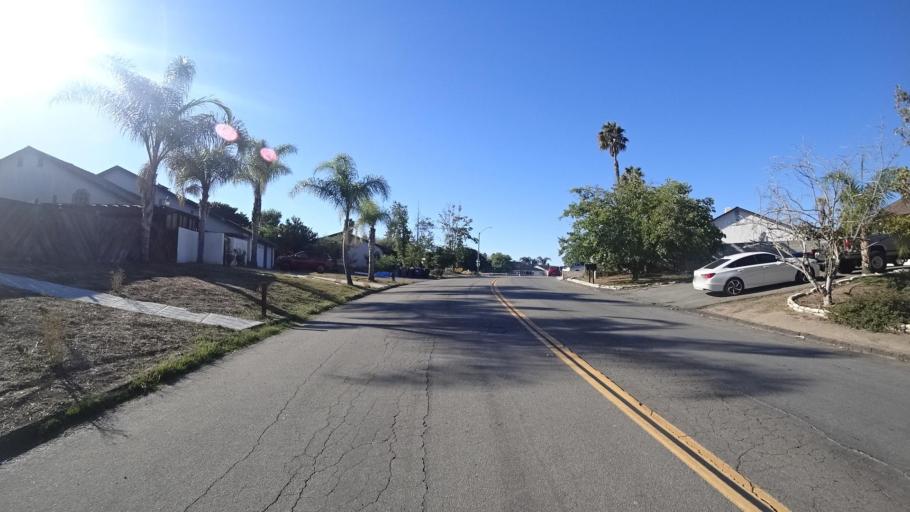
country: US
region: California
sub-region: San Diego County
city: Bonita
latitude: 32.6861
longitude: -117.0226
